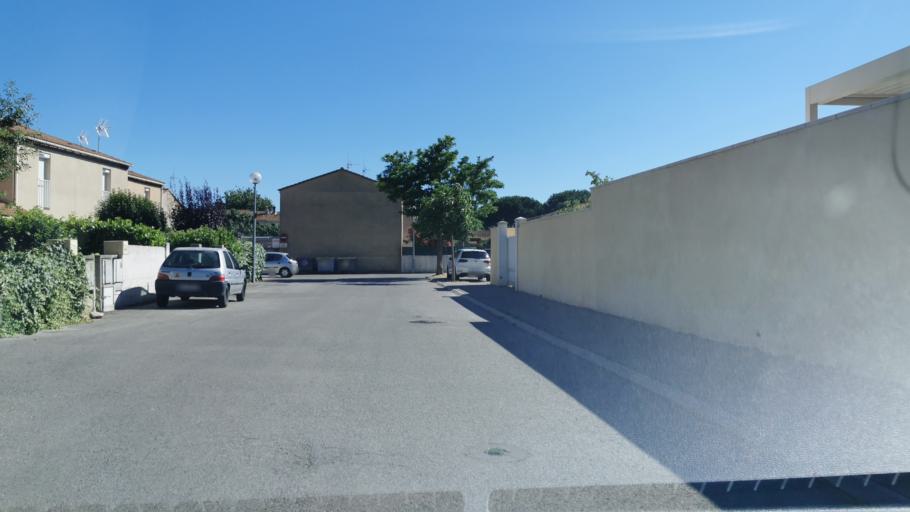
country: FR
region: Languedoc-Roussillon
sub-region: Departement de l'Aude
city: Narbonne
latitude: 43.1979
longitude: 3.0170
